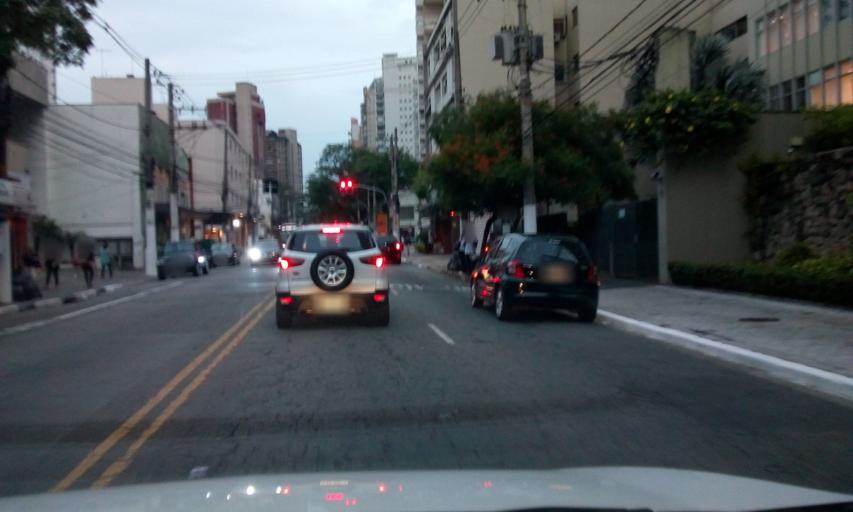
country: BR
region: Sao Paulo
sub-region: Sao Paulo
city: Sao Paulo
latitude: -23.5954
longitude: -46.6691
